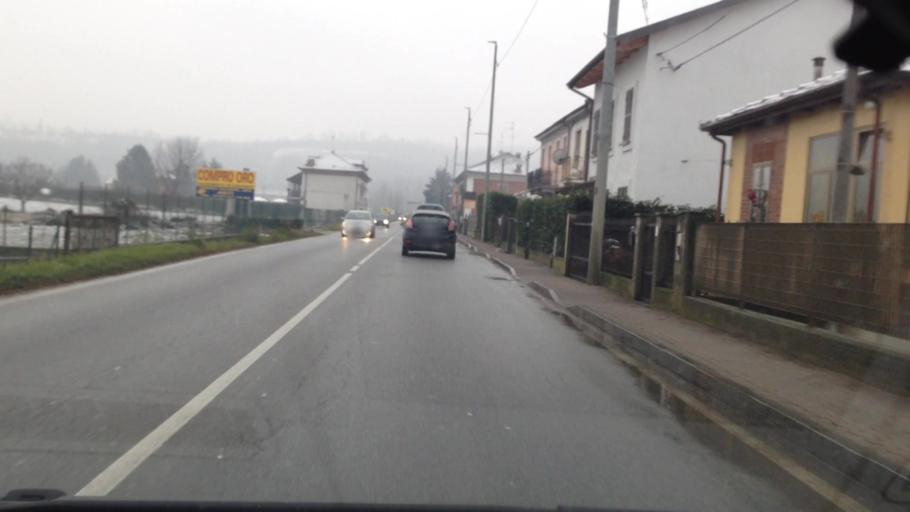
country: IT
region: Piedmont
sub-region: Provincia di Asti
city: Asti
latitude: 44.8812
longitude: 8.2133
